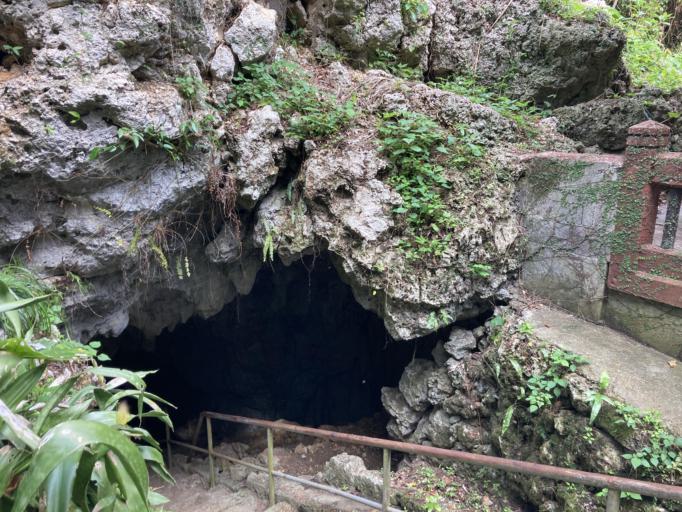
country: JP
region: Okinawa
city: Itoman
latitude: 26.1164
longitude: 127.6867
